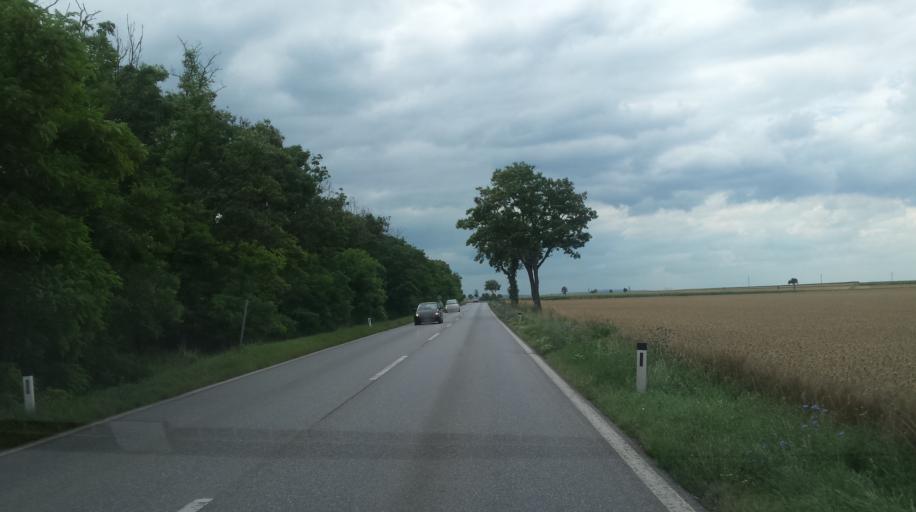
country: AT
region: Lower Austria
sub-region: Politischer Bezirk Wien-Umgebung
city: Moosbrunn
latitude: 48.0522
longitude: 16.4610
